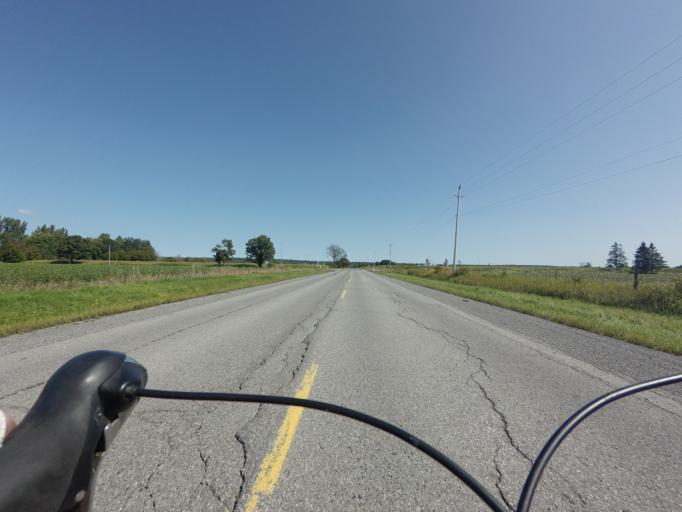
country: CA
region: Ontario
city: Carleton Place
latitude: 45.3379
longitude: -76.0759
